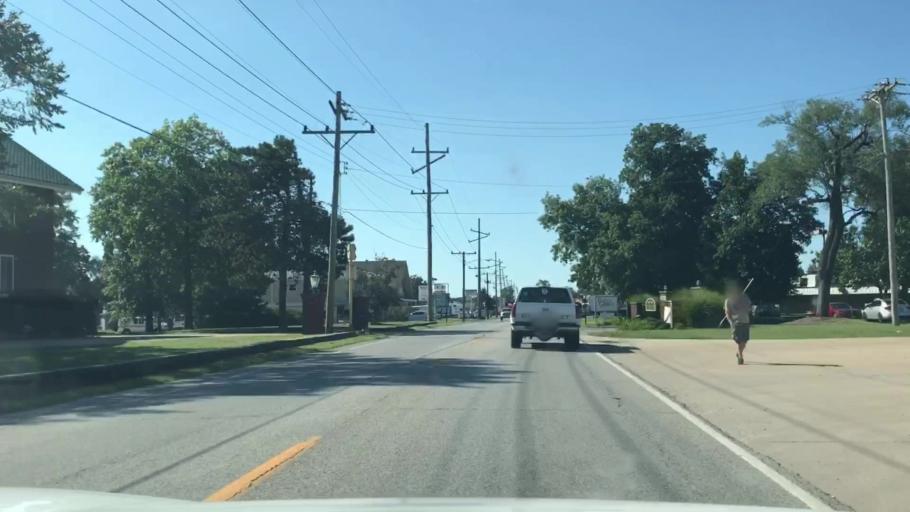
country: US
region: Illinois
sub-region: Madison County
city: Wood River
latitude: 38.8685
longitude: -90.0883
